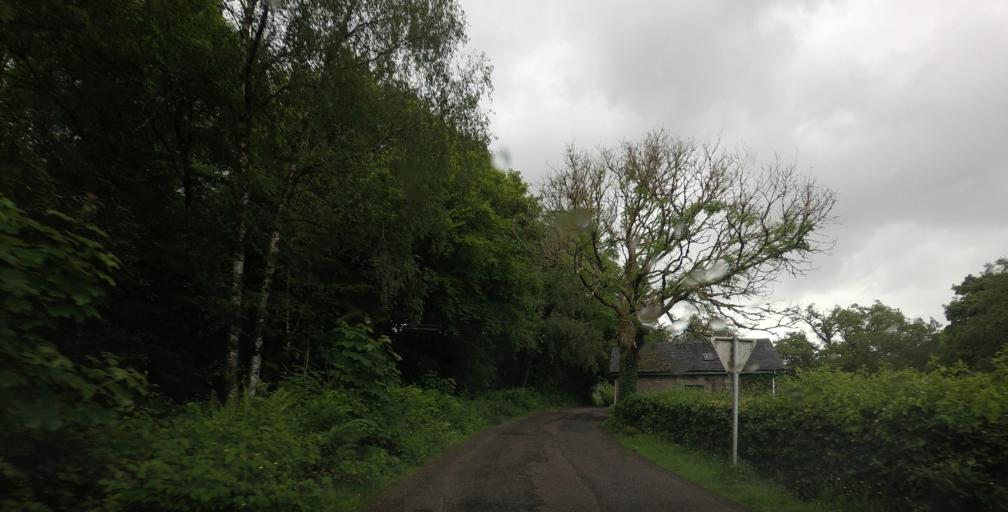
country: GB
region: Scotland
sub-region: Argyll and Bute
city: Oban
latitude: 56.6960
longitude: -5.5724
